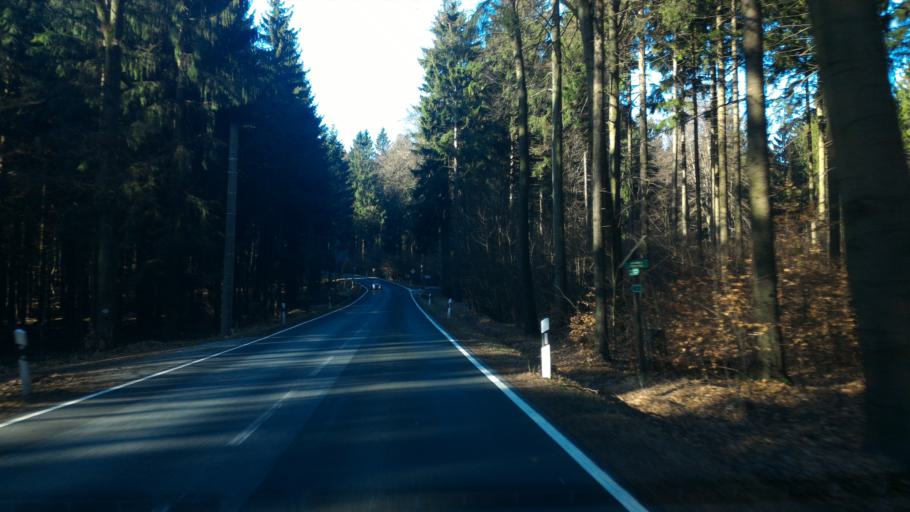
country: DE
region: Saxony
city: Neukirch/Lausitz
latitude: 51.0556
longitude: 14.2852
